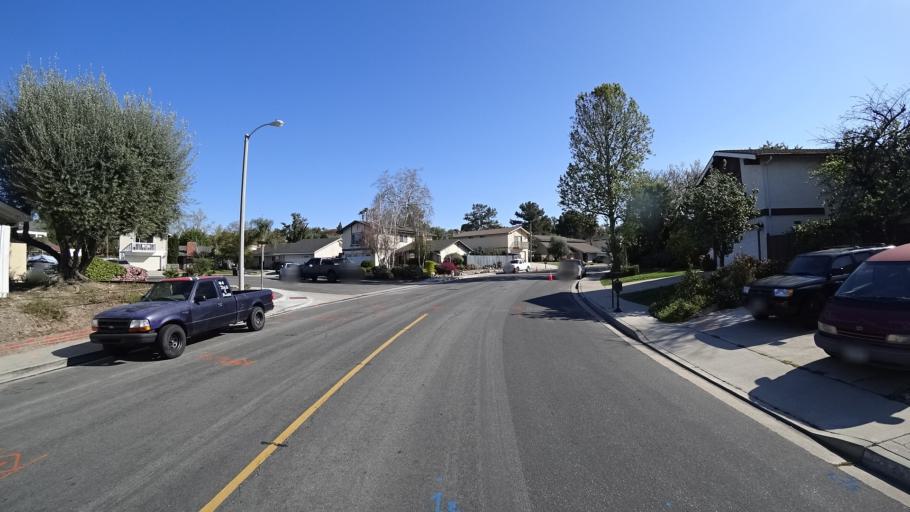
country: US
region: California
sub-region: Ventura County
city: Thousand Oaks
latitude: 34.2110
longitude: -118.8390
